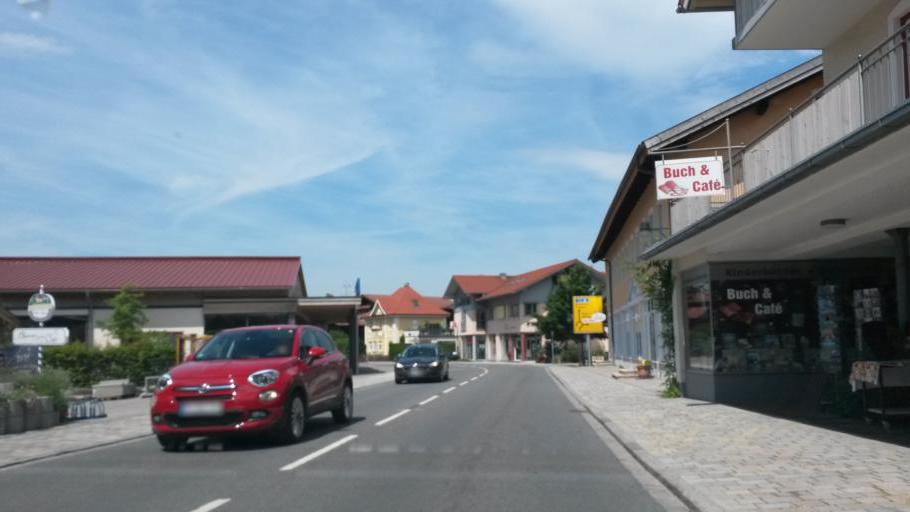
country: DE
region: Bavaria
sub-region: Upper Bavaria
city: Aschau im Chiemgau
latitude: 47.7795
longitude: 12.3247
